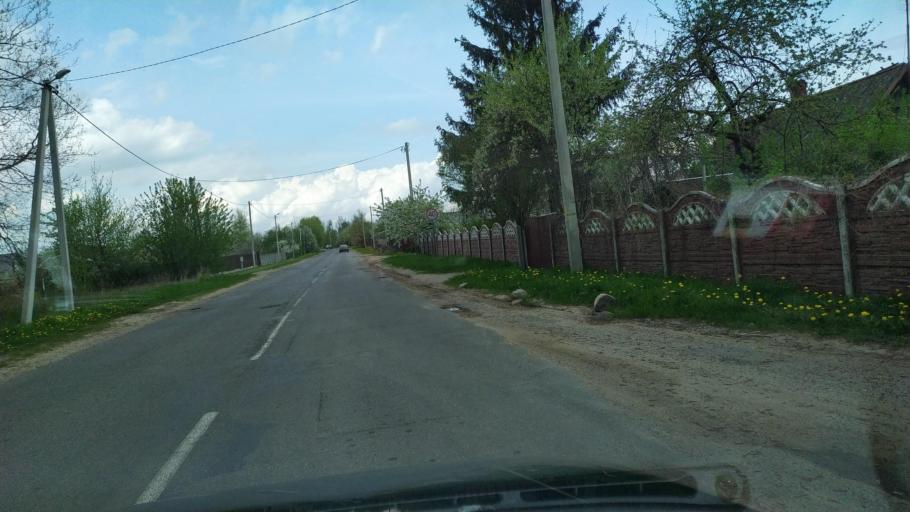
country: BY
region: Brest
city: Pruzhany
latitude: 52.5849
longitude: 24.4113
